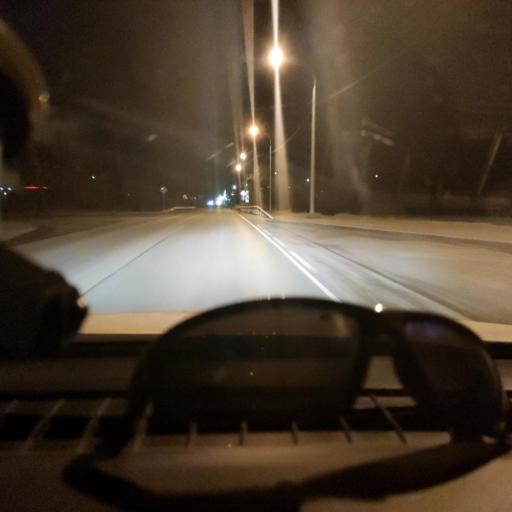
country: RU
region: Samara
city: Chapayevsk
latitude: 52.9945
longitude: 49.7236
